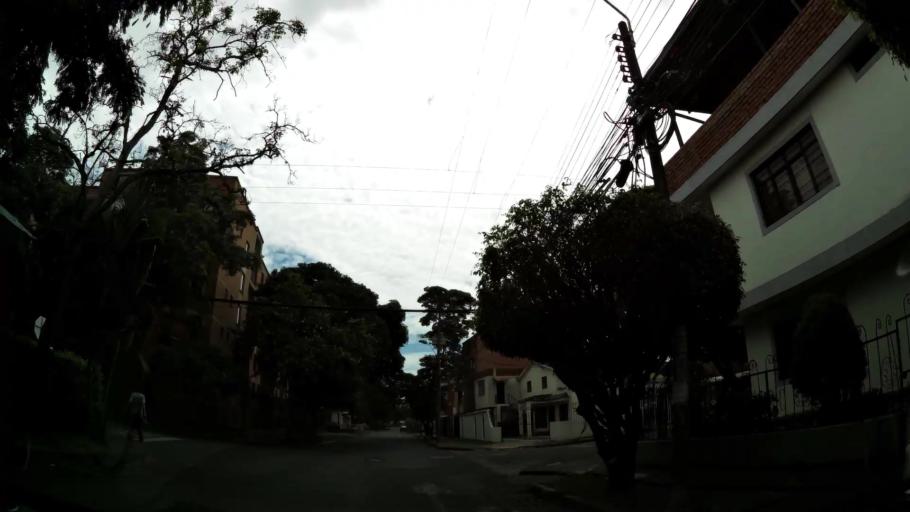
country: CO
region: Valle del Cauca
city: Cali
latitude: 3.3996
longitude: -76.5484
